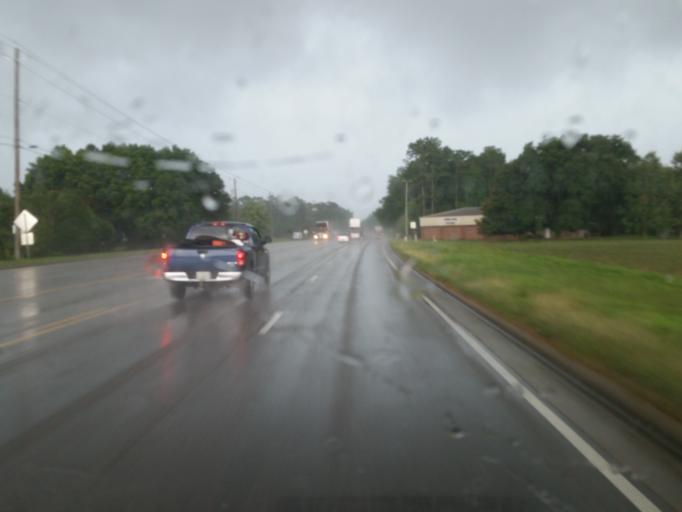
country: US
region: Alabama
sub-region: Mobile County
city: Prichard
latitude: 30.7831
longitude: -88.2736
